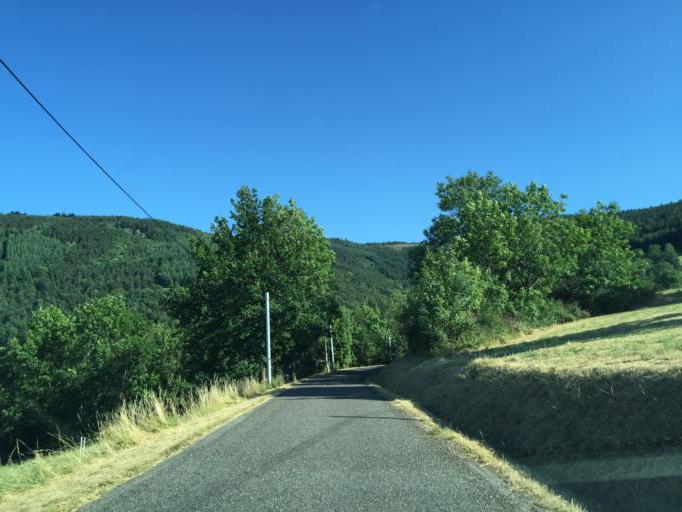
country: FR
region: Rhone-Alpes
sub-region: Departement de la Loire
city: Saint-Jean-Bonnefonds
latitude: 45.4334
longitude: 4.4788
